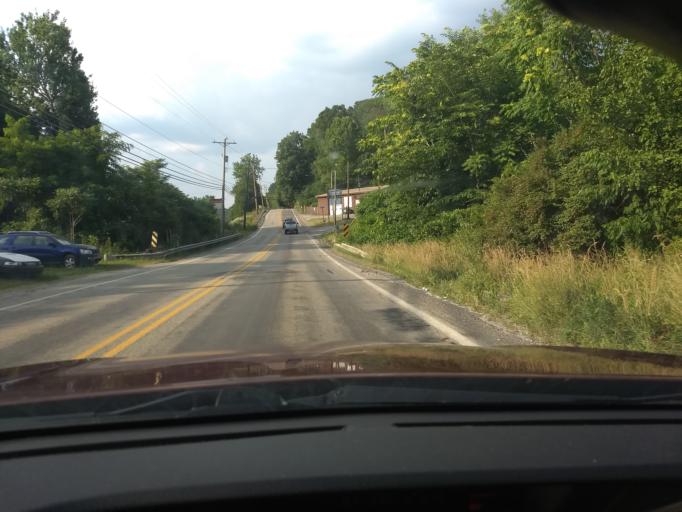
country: US
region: Pennsylvania
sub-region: Westmoreland County
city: Lower Burrell
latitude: 40.5427
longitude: -79.7611
